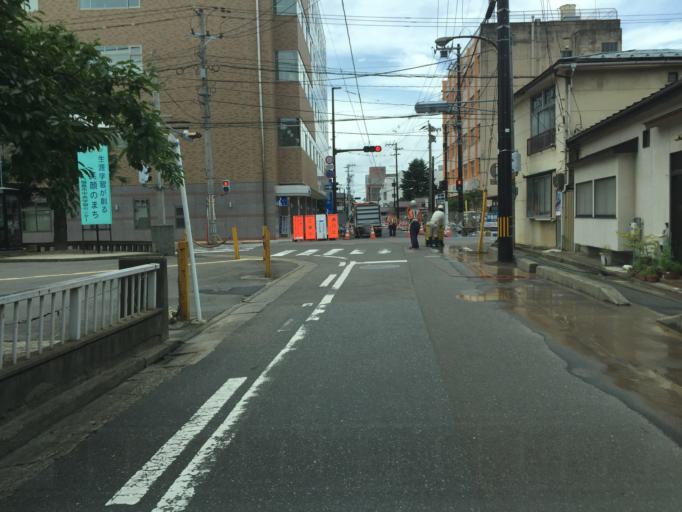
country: JP
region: Fukushima
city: Fukushima-shi
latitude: 37.7578
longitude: 140.4702
